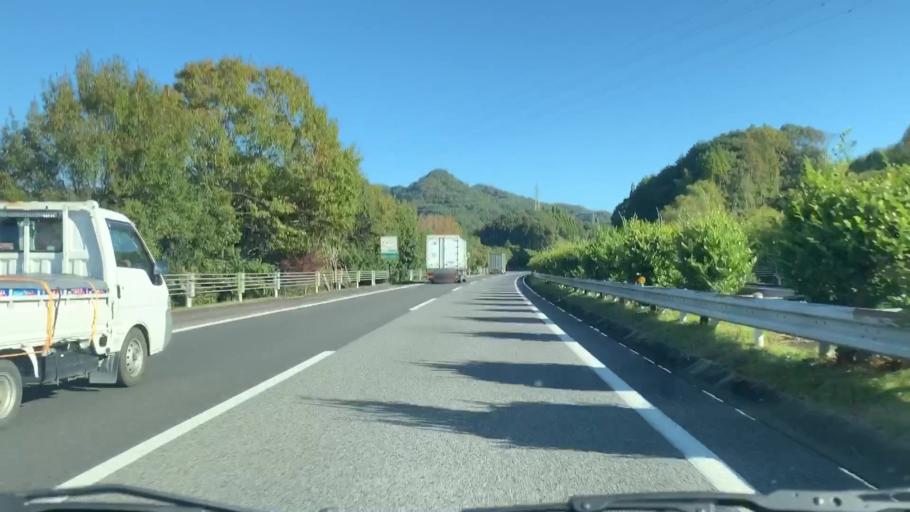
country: JP
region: Saga Prefecture
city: Takeocho-takeo
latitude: 33.2261
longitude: 130.0508
